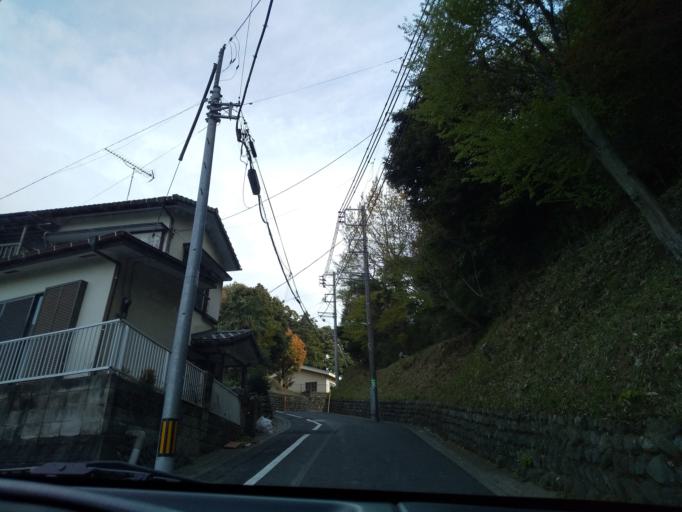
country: JP
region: Tokyo
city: Hino
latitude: 35.6526
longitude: 139.4276
